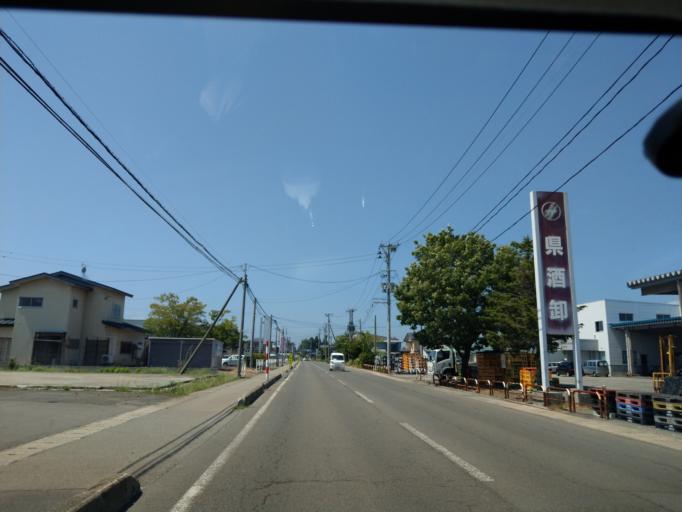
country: JP
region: Akita
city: Yokotemachi
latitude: 39.3194
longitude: 140.5457
